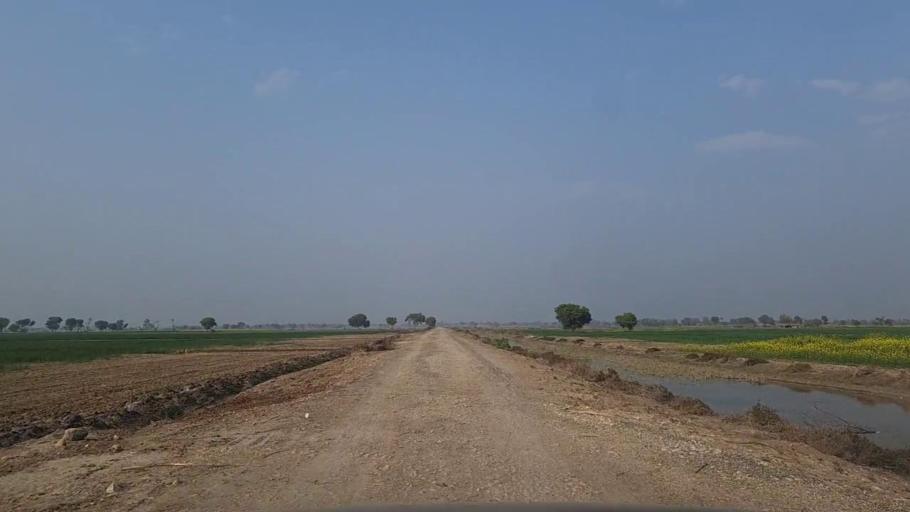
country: PK
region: Sindh
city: Nawabshah
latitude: 26.3361
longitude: 68.4737
